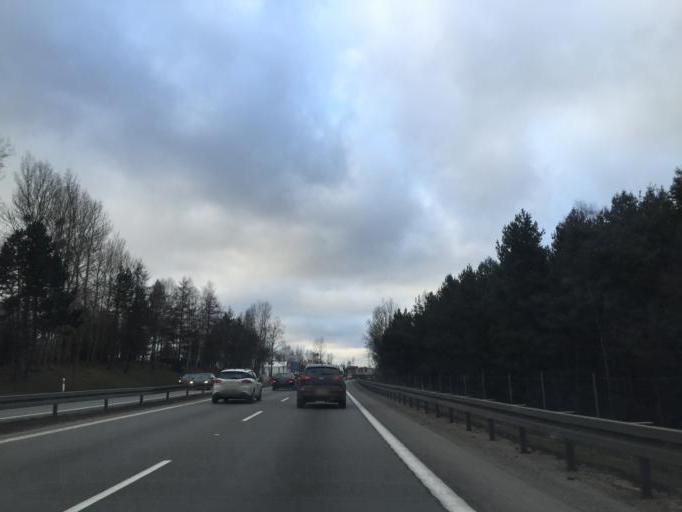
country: PL
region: Pomeranian Voivodeship
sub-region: Gdynia
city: Wielki Kack
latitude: 54.3934
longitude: 18.4895
